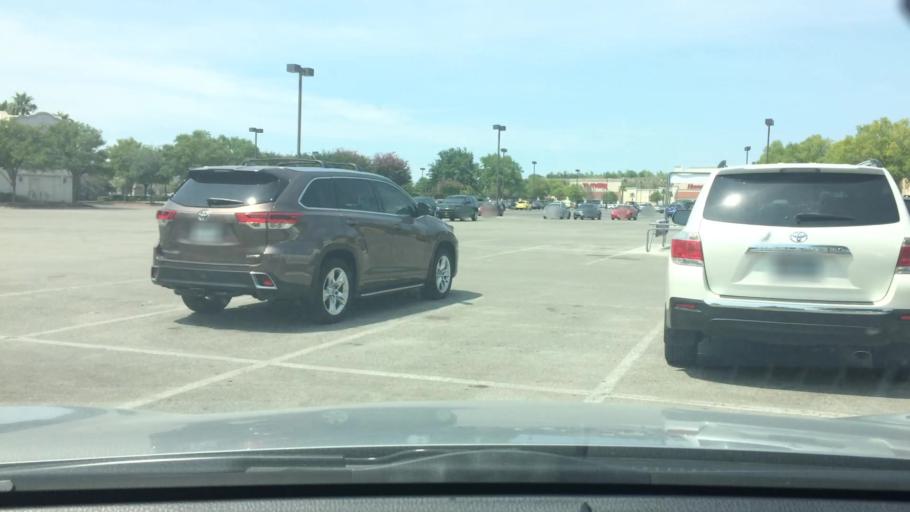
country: US
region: Texas
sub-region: Bexar County
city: Shavano Park
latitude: 29.6075
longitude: -98.5957
